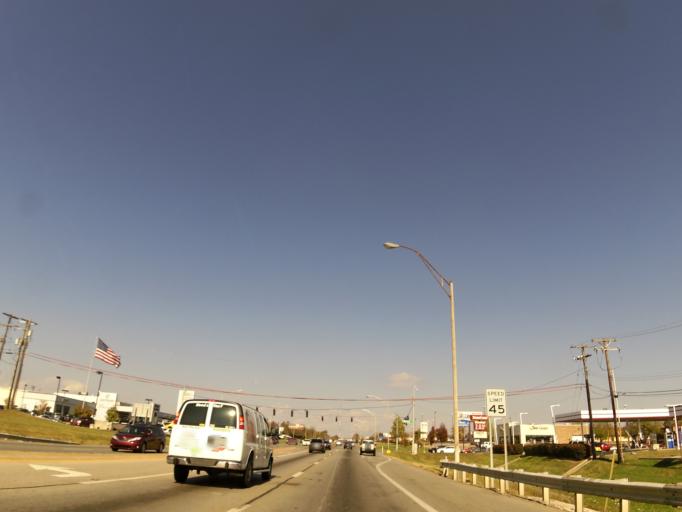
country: US
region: Kentucky
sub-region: Fayette County
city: Lexington-Fayette
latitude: 38.0168
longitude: -84.4568
